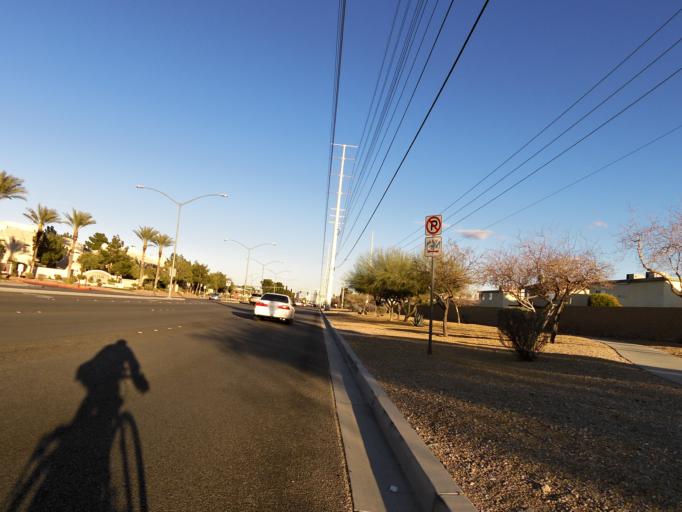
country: US
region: Nevada
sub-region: Clark County
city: Spring Valley
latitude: 36.1145
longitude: -115.2544
